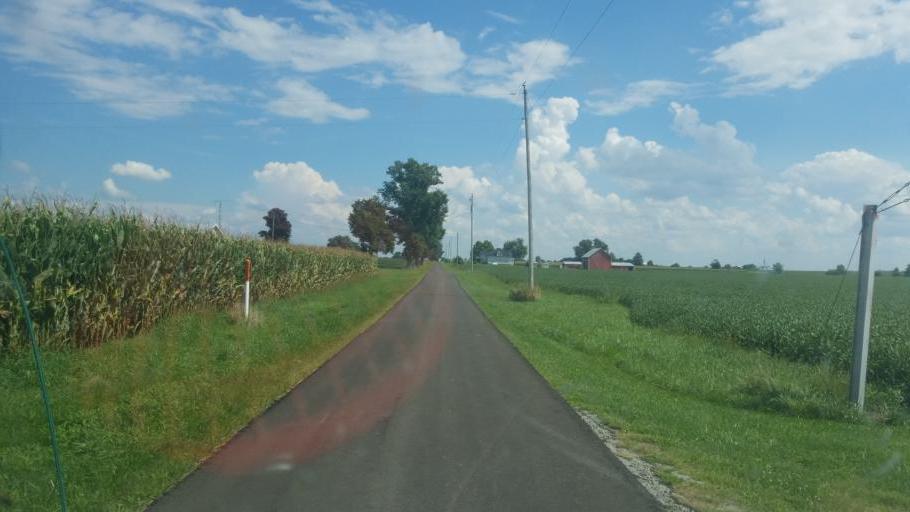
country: US
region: Ohio
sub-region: Hardin County
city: Forest
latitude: 40.8470
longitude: -83.4533
